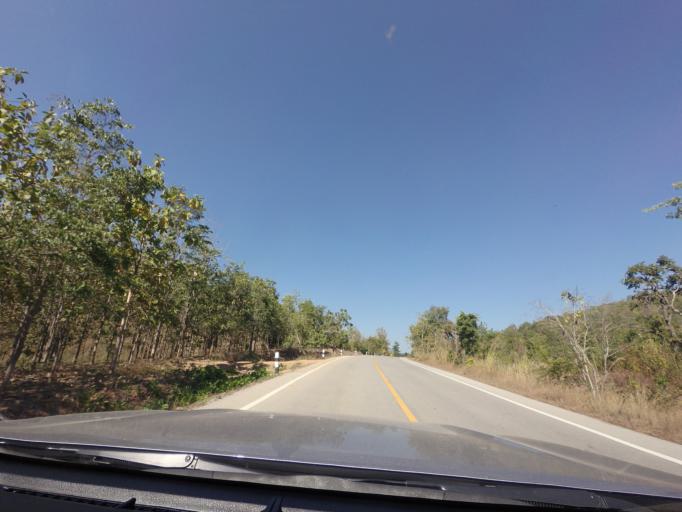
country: TH
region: Lampang
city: Chae Hom
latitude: 18.5651
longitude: 99.6235
